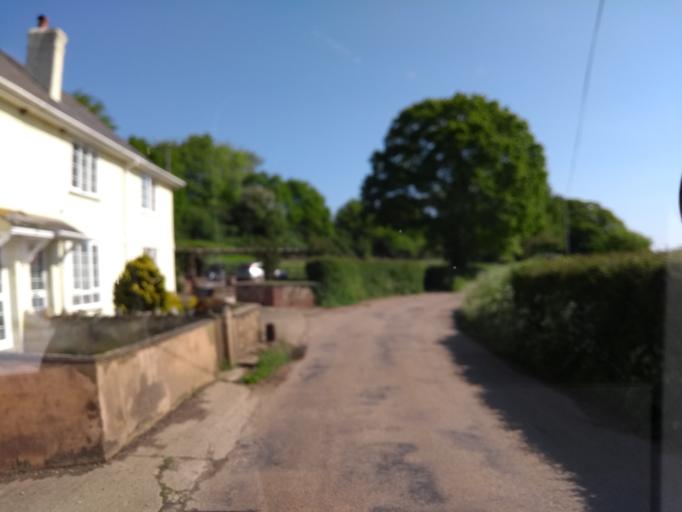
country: GB
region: England
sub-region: Devon
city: Colyton
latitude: 50.7588
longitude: -3.0443
